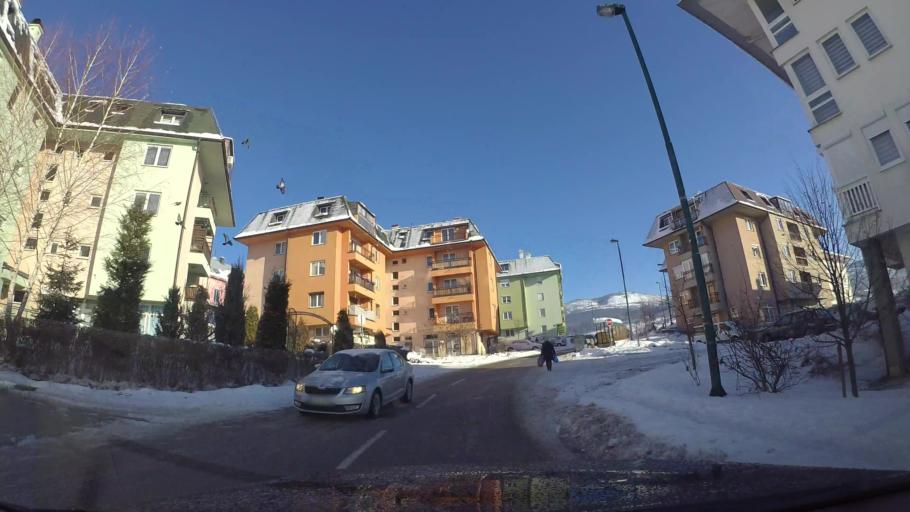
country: BA
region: Federation of Bosnia and Herzegovina
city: Kobilja Glava
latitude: 43.8805
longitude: 18.3996
